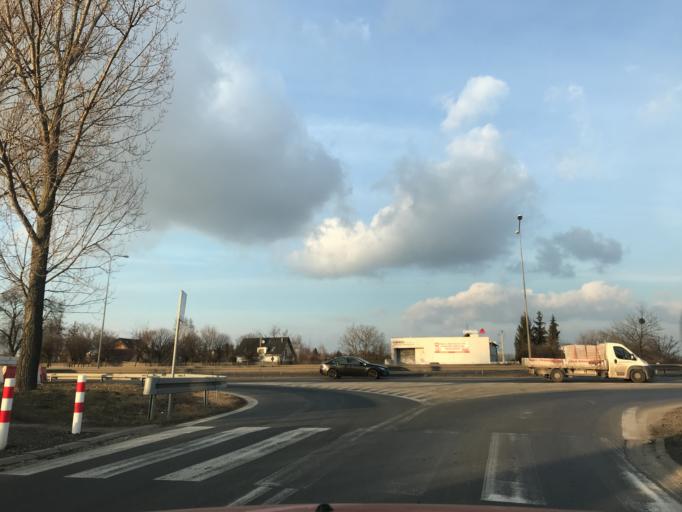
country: PL
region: Greater Poland Voivodeship
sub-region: Powiat poznanski
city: Baranowo
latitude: 52.4474
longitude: 16.7268
